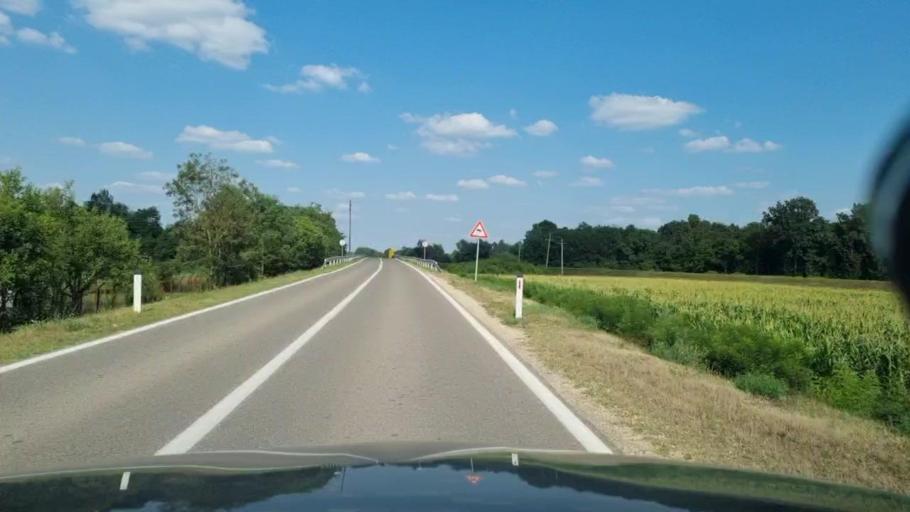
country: BA
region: Federation of Bosnia and Herzegovina
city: Odzak
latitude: 45.1067
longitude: 18.2770
